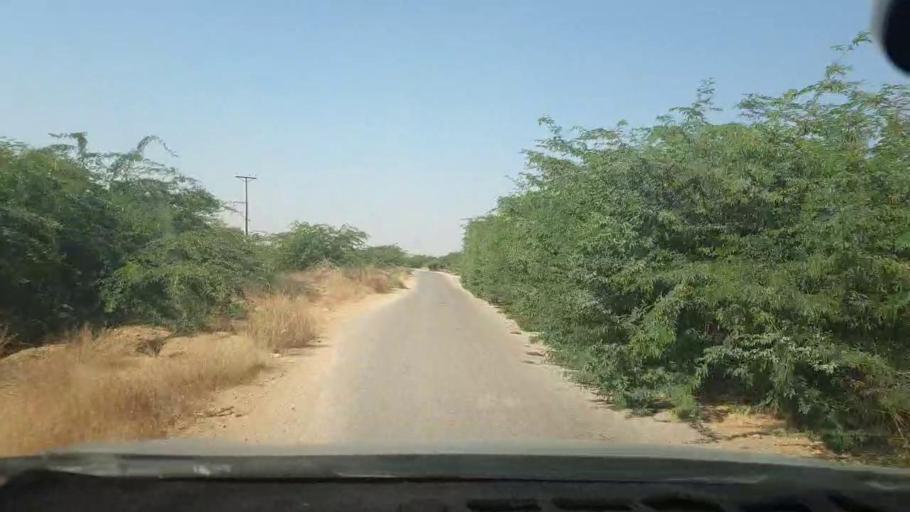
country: PK
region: Sindh
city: Malir Cantonment
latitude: 25.1569
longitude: 67.1437
